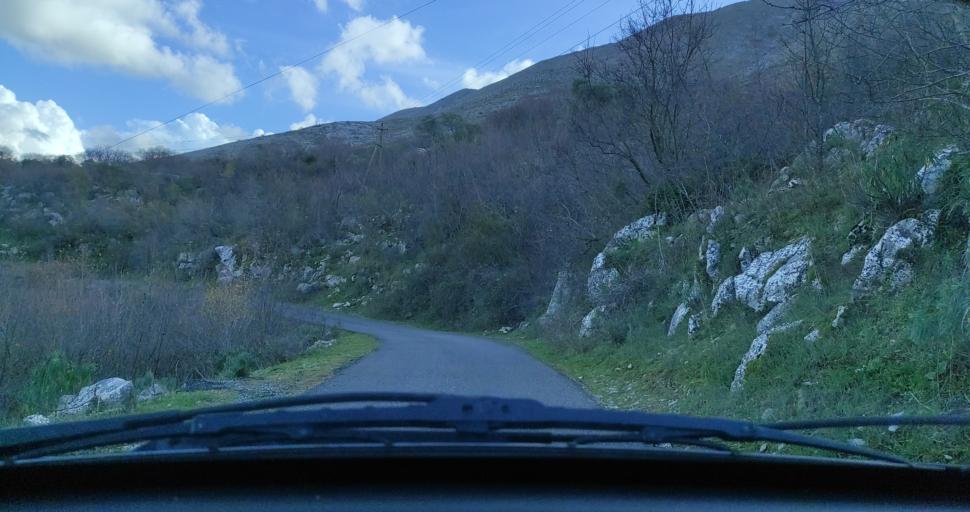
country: AL
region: Shkoder
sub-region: Rrethi i Shkodres
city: Dajc
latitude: 42.0687
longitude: 19.4137
